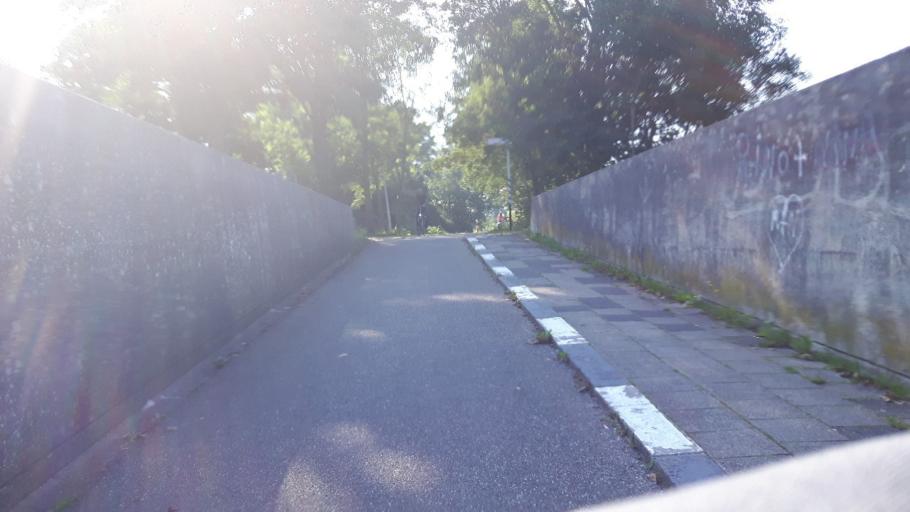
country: NL
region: Friesland
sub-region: Gemeente Franekeradeel
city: Franeker
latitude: 53.1908
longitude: 5.5532
